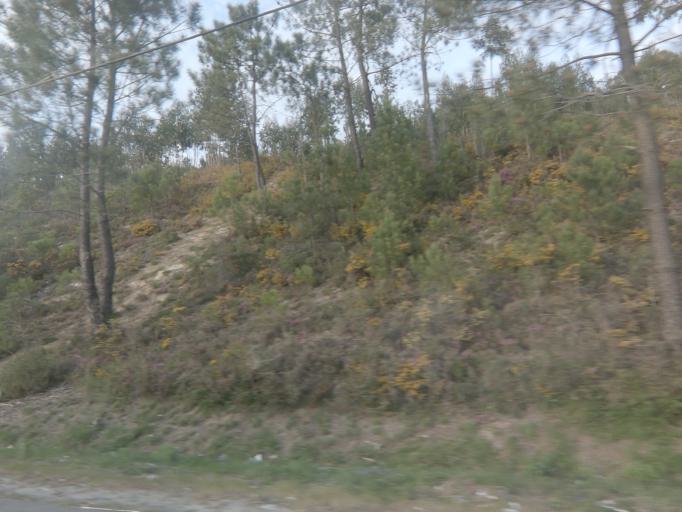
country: PT
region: Porto
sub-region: Valongo
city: Valongo
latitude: 41.1997
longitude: -8.5248
